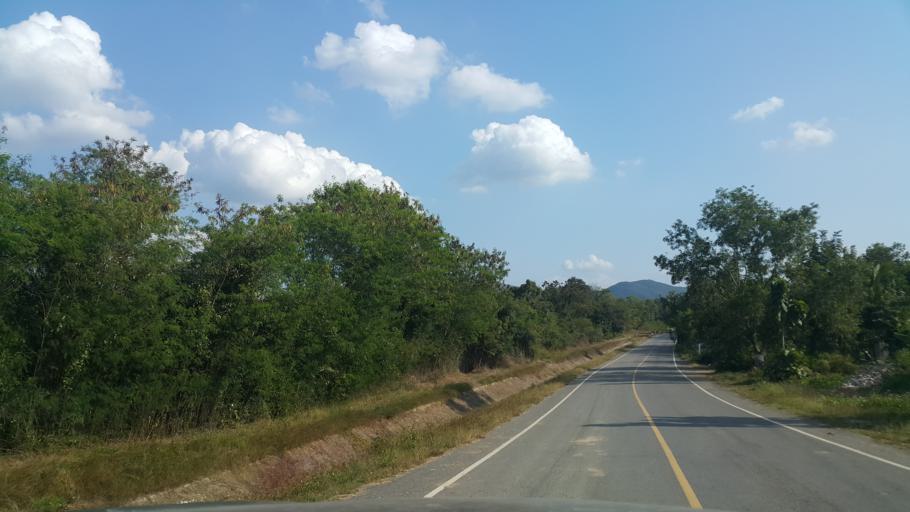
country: TH
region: Lamphun
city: Mae Tha
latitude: 18.5282
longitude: 99.0998
